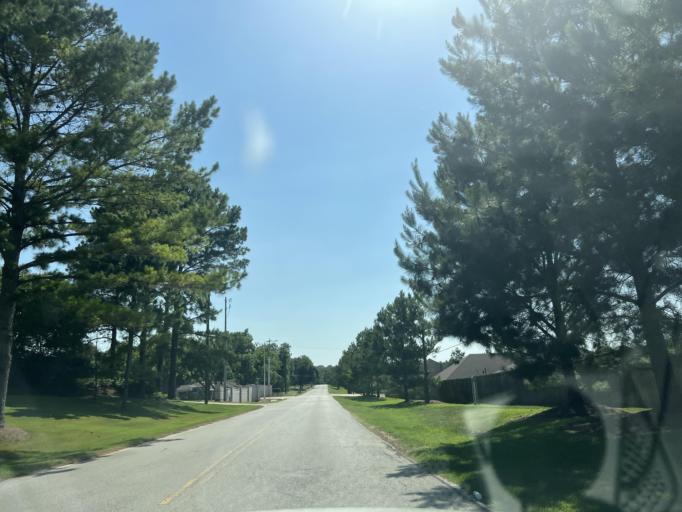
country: US
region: Texas
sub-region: Washington County
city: Brenham
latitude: 30.1519
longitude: -96.3701
